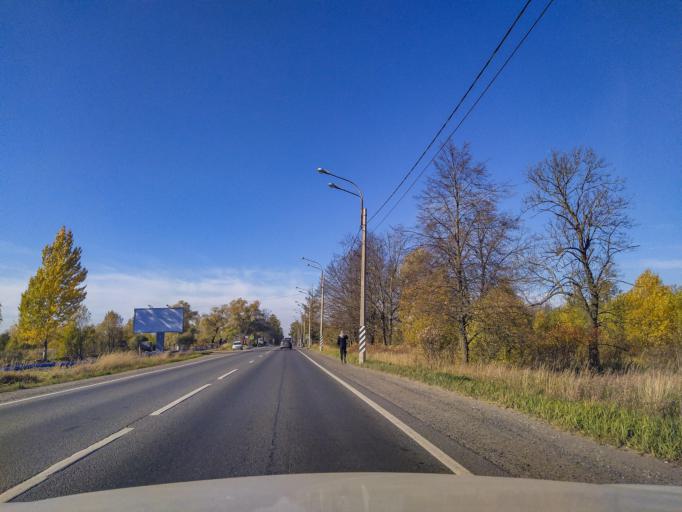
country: RU
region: St.-Petersburg
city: Aleksandrovskaya
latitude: 59.7042
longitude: 30.3467
